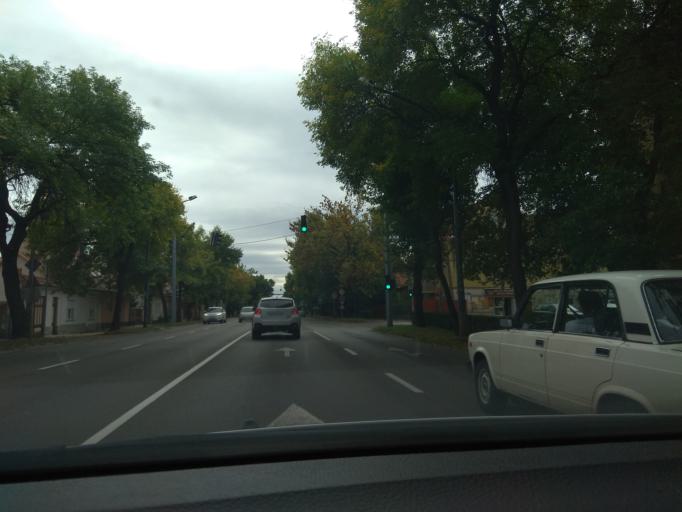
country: HU
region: Heves
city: Eger
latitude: 47.8826
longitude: 20.3814
